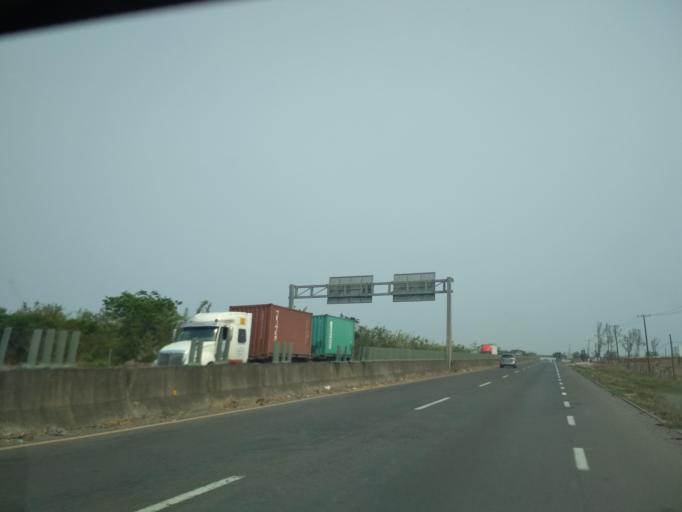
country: MX
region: Veracruz
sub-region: Veracruz
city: Delfino Victoria (Santa Fe)
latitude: 19.1801
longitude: -96.2712
